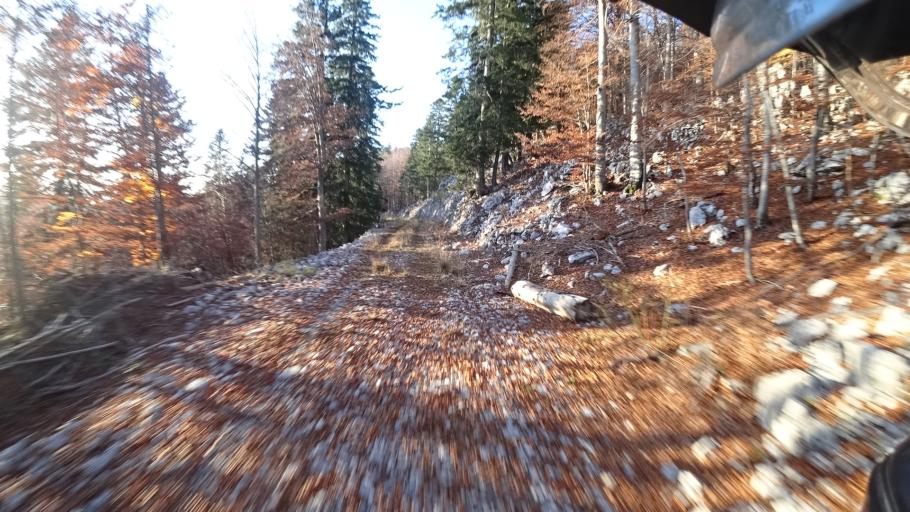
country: HR
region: Primorsko-Goranska
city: Drazice
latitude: 45.4816
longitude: 14.4916
